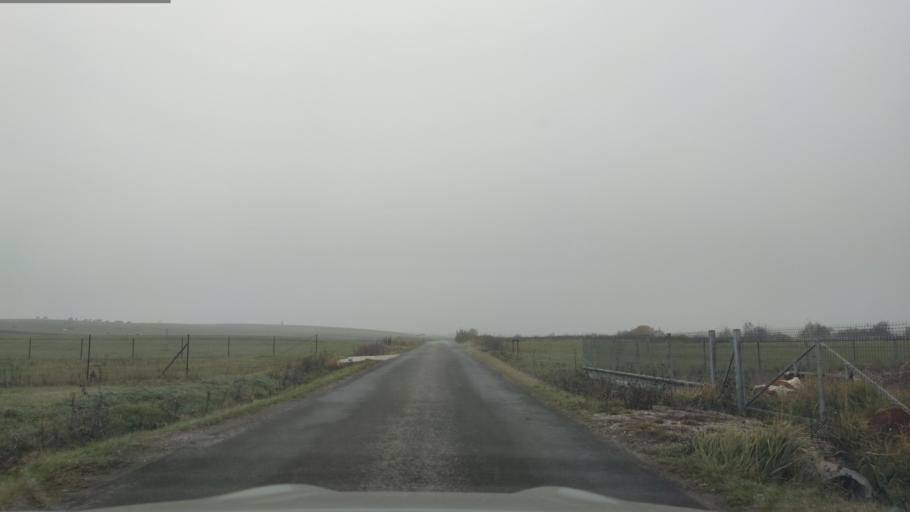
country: RO
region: Harghita
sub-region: Comuna Remetea
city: Remetea
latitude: 46.8034
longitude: 25.4344
